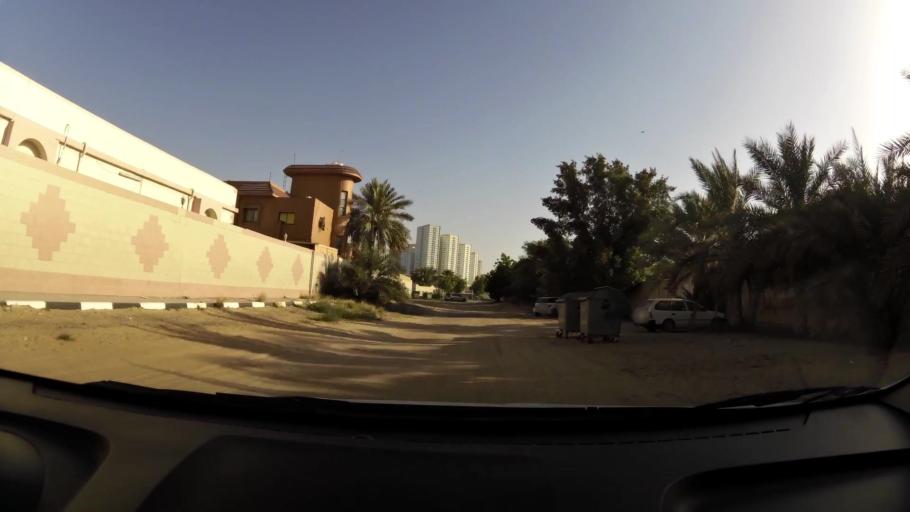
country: AE
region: Ajman
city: Ajman
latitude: 25.3997
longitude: 55.4713
